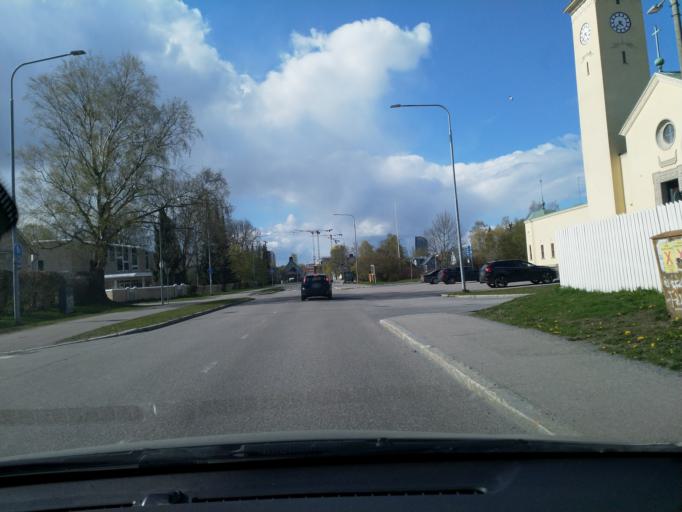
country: FI
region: Pirkanmaa
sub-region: Tampere
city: Tampere
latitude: 61.4858
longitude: 23.7854
